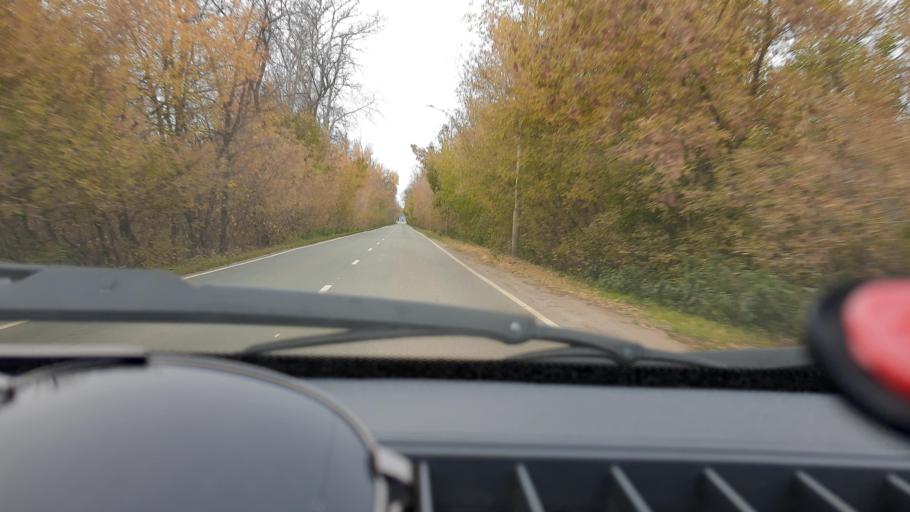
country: RU
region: Bashkortostan
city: Ufa
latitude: 54.6634
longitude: 55.9377
